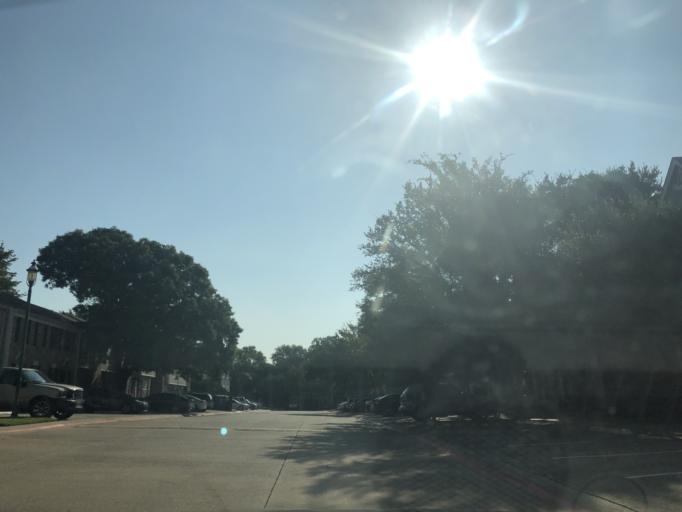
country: US
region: Texas
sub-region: Tarrant County
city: Euless
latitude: 32.8681
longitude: -97.0820
